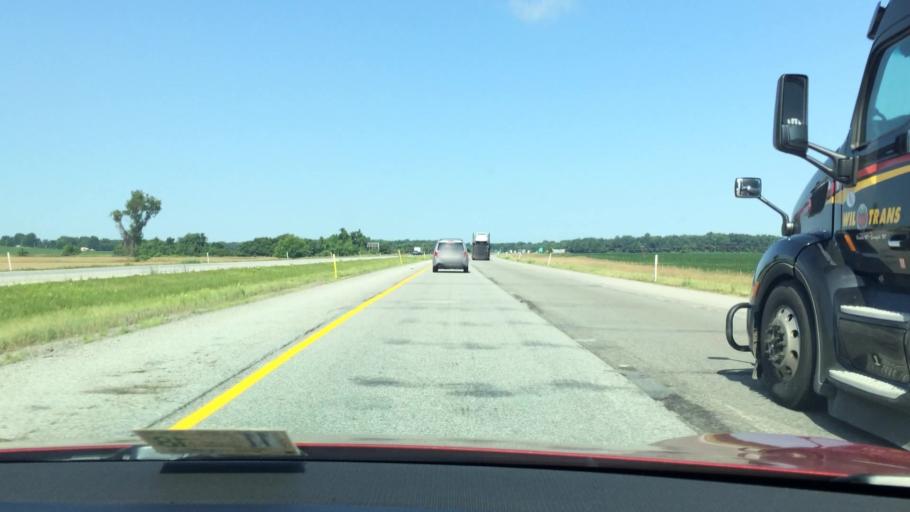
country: US
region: Michigan
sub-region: Saint Joseph County
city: White Pigeon
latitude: 41.7517
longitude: -85.6258
